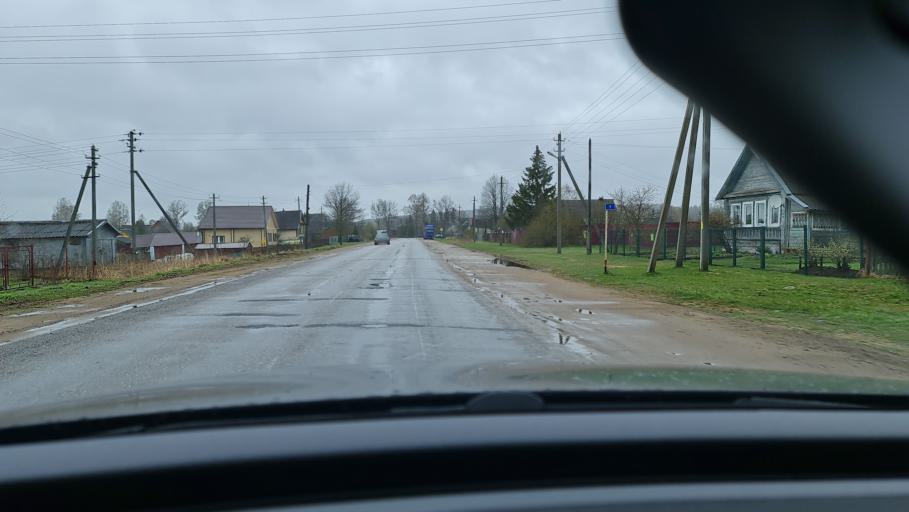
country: RU
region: Novgorod
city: Valday
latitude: 58.0344
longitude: 32.9647
